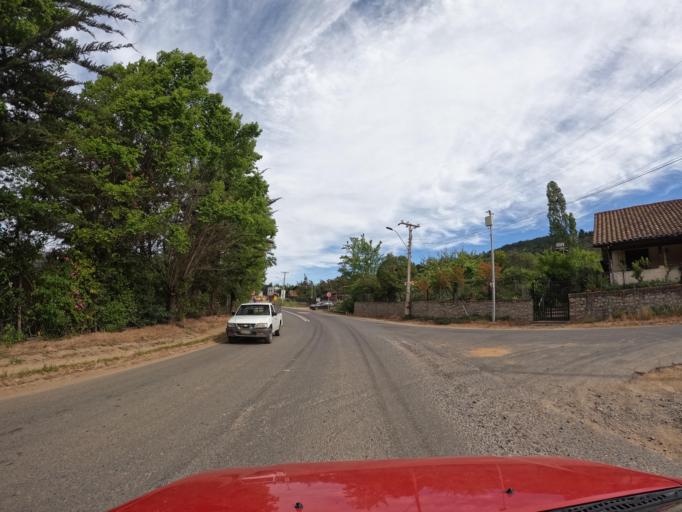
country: CL
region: Maule
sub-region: Provincia de Talca
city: Talca
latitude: -35.3201
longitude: -71.9580
